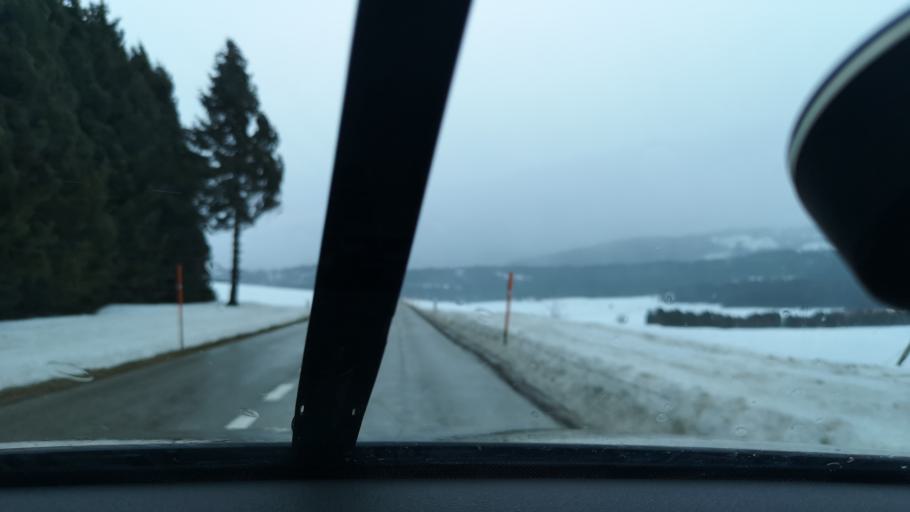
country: FR
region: Franche-Comte
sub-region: Departement du Doubs
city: Les Fourgs
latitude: 46.8193
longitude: 6.4425
